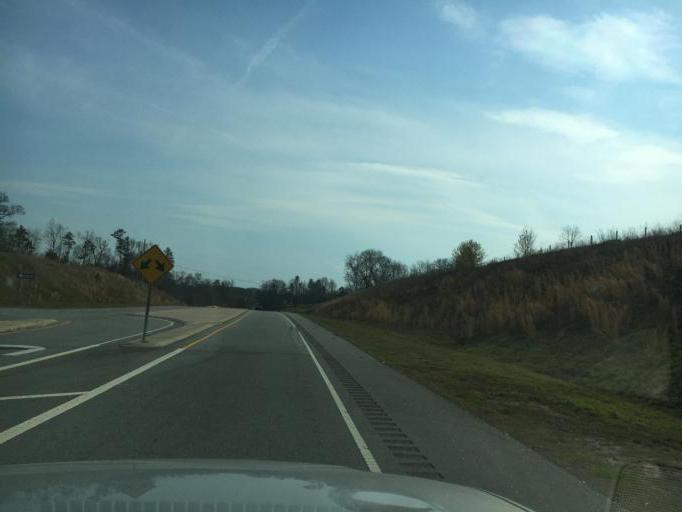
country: US
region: South Carolina
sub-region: Spartanburg County
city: Mayo
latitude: 35.1876
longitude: -81.8433
